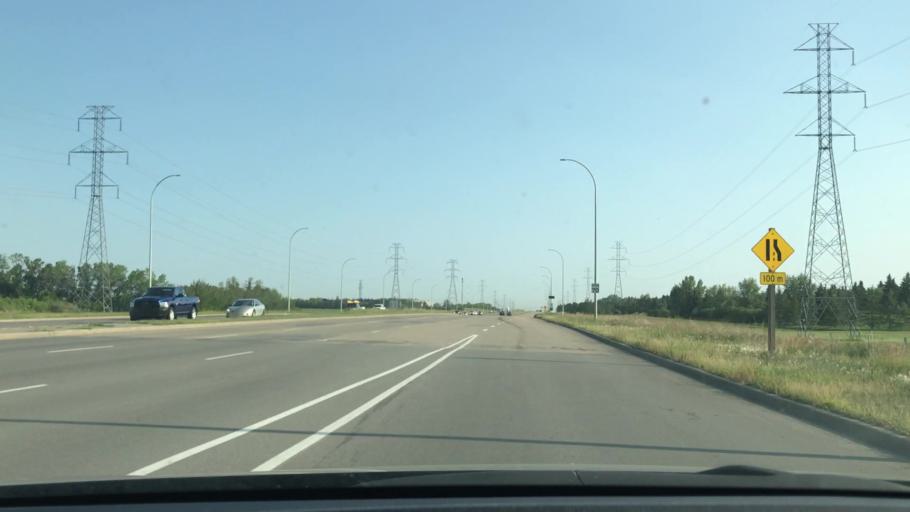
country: CA
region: Alberta
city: Beaumont
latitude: 53.4403
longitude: -113.4664
